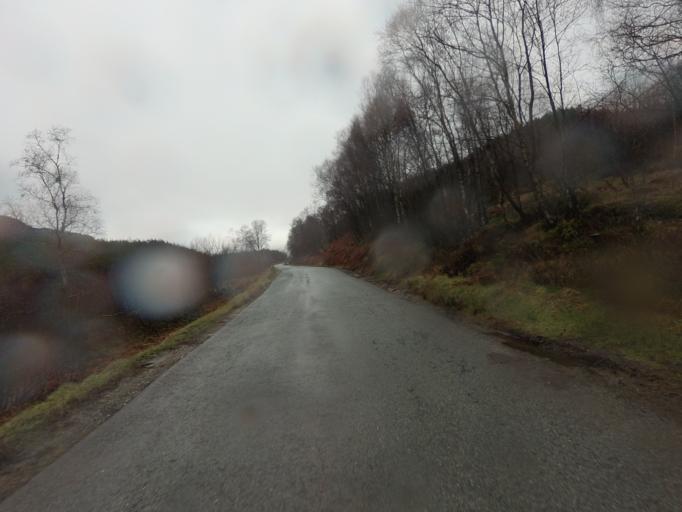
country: GB
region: Scotland
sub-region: West Dunbartonshire
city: Balloch
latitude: 56.2399
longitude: -4.5671
